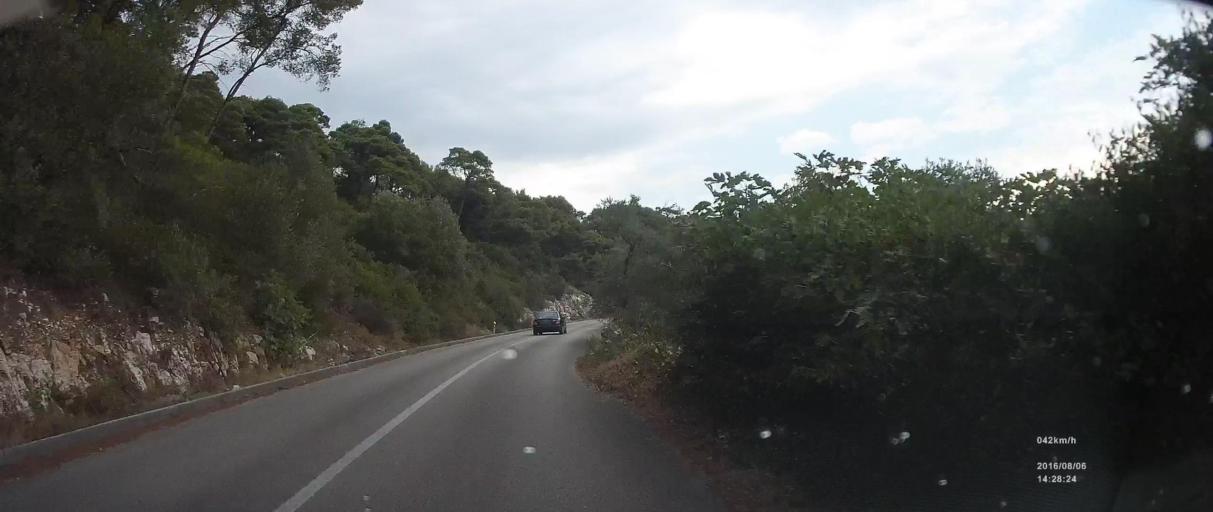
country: HR
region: Dubrovacko-Neretvanska
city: Ston
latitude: 42.7035
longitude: 17.7363
